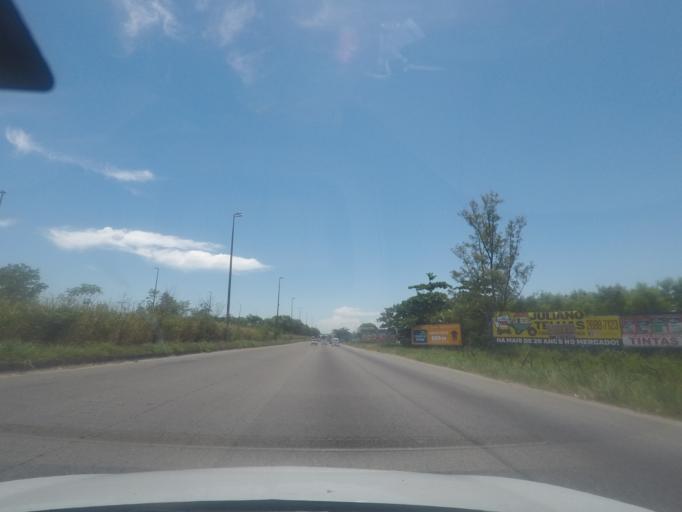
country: BR
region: Rio de Janeiro
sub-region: Itaguai
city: Itaguai
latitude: -22.8904
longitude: -43.6653
